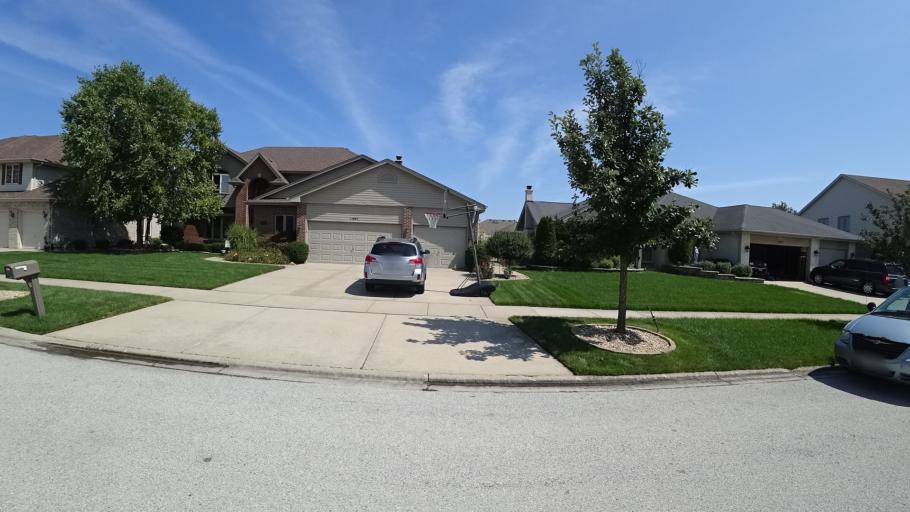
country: US
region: Illinois
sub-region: Cook County
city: Orland Hills
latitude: 41.5633
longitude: -87.8293
